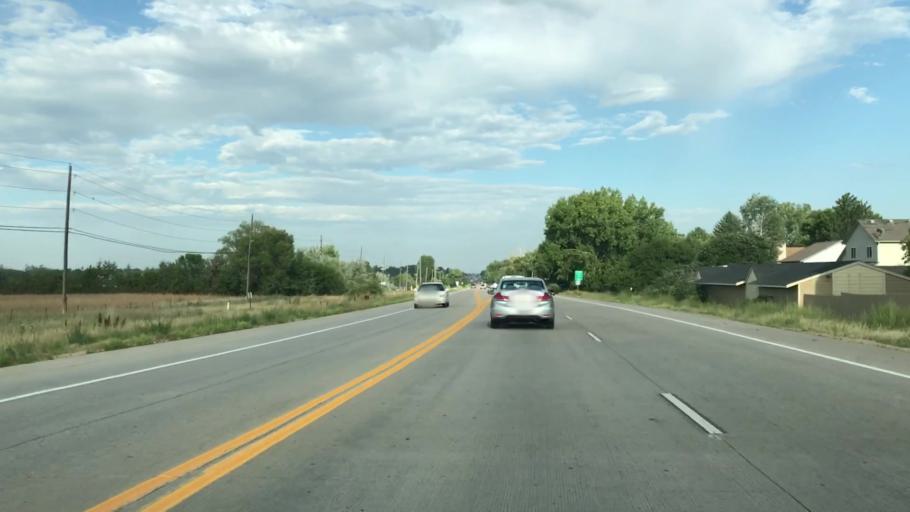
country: US
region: Colorado
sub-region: Boulder County
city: Longmont
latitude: 40.2032
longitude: -105.1280
